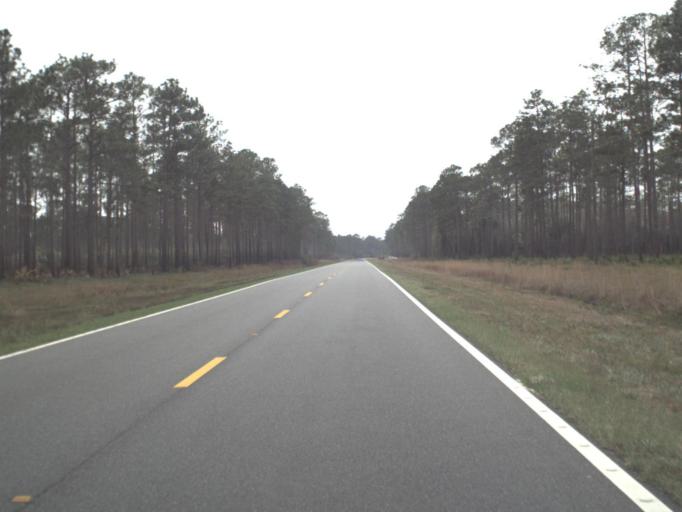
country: US
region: Florida
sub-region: Liberty County
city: Bristol
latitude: 30.2673
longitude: -84.8503
